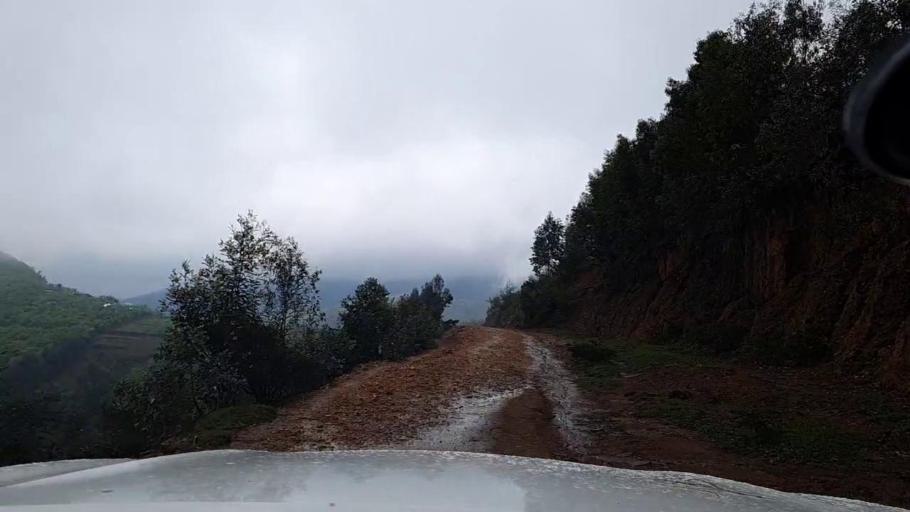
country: RW
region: Western Province
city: Kibuye
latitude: -2.1438
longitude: 29.4592
